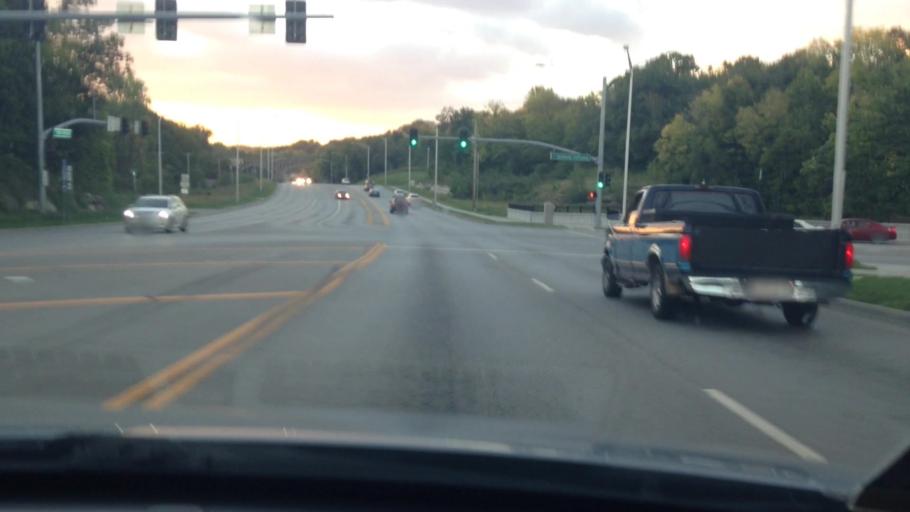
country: US
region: Missouri
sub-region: Jackson County
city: Raytown
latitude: 39.0291
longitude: -94.5084
